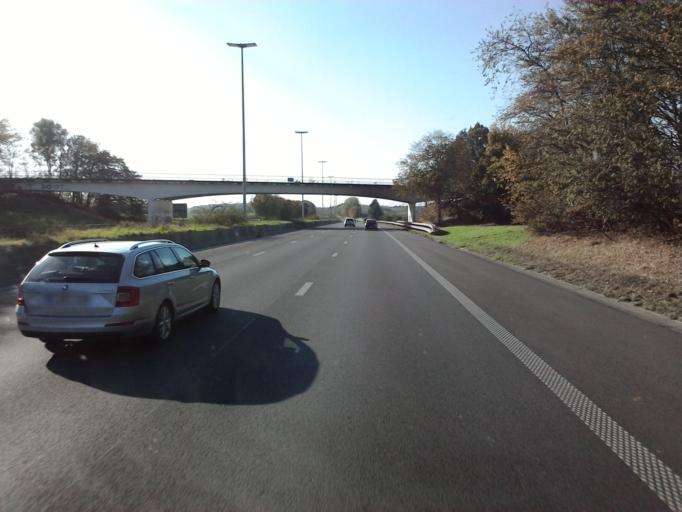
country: BE
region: Wallonia
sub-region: Province de Namur
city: Sombreffe
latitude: 50.4943
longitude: 4.6445
